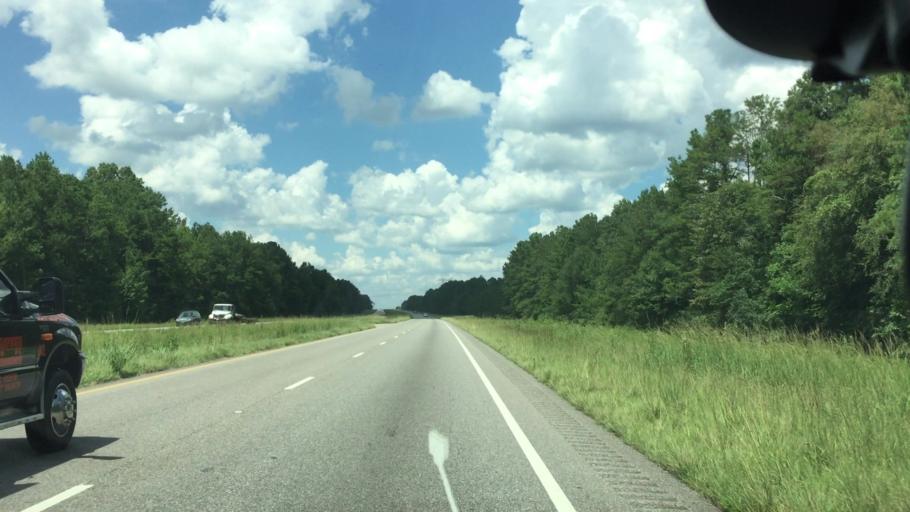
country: US
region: Alabama
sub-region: Pike County
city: Troy
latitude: 31.9961
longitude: -86.0270
